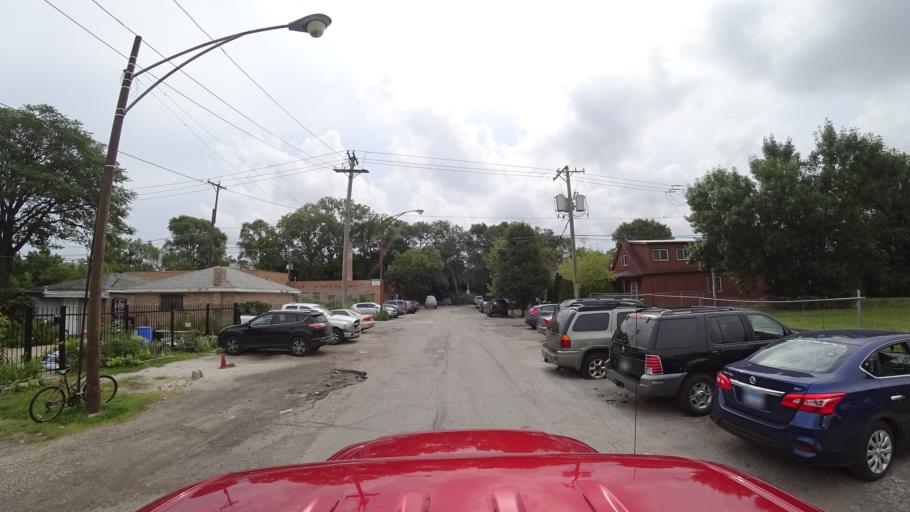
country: US
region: Illinois
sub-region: Cook County
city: Chicago
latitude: 41.8193
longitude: -87.6838
